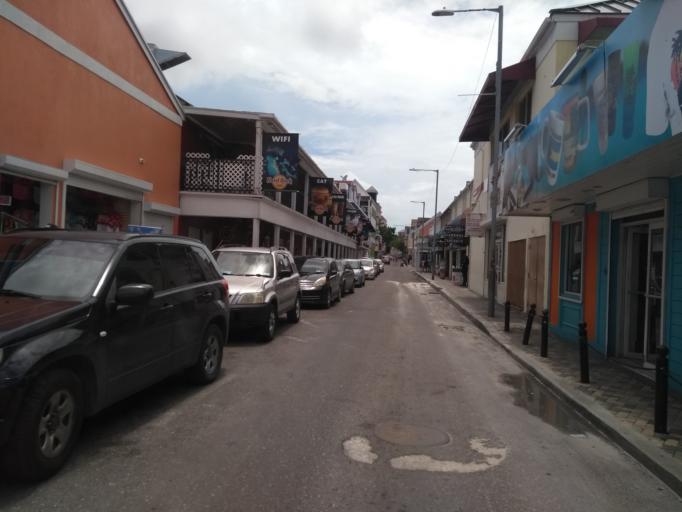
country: BS
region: New Providence
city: Nassau
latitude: 25.0787
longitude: -77.3418
